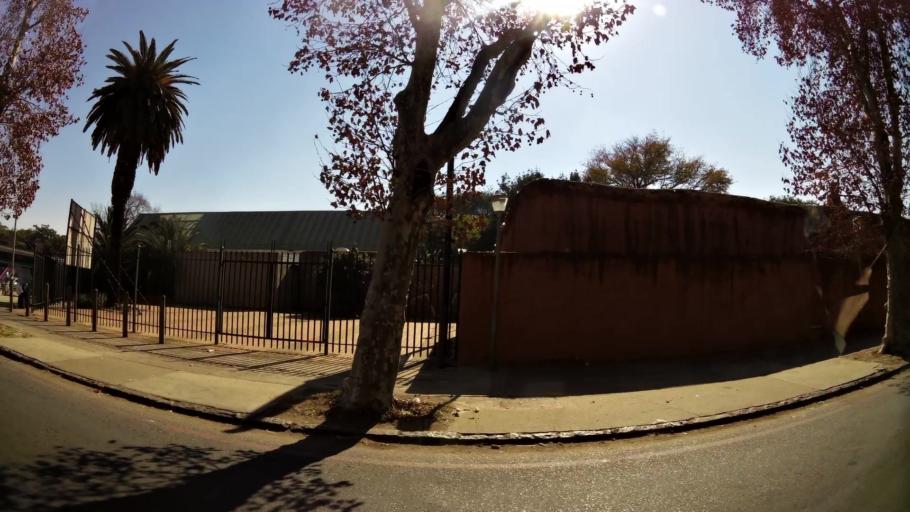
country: ZA
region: Gauteng
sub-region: City of Tshwane Metropolitan Municipality
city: Pretoria
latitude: -25.7391
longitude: 28.1880
